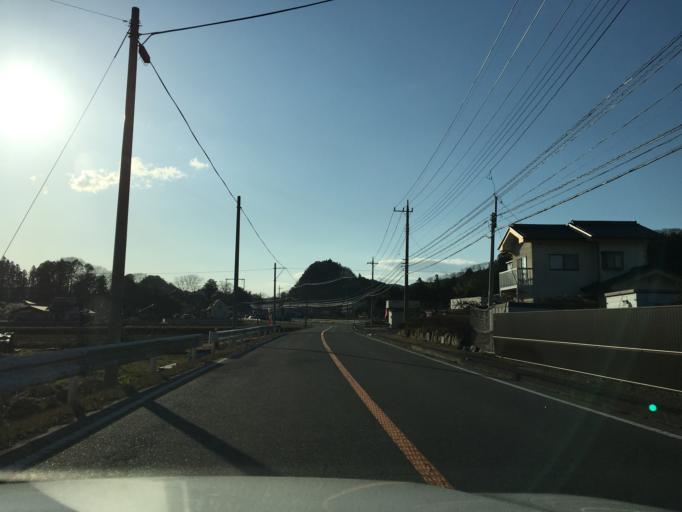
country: JP
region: Ibaraki
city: Daigo
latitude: 36.7778
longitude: 140.3018
